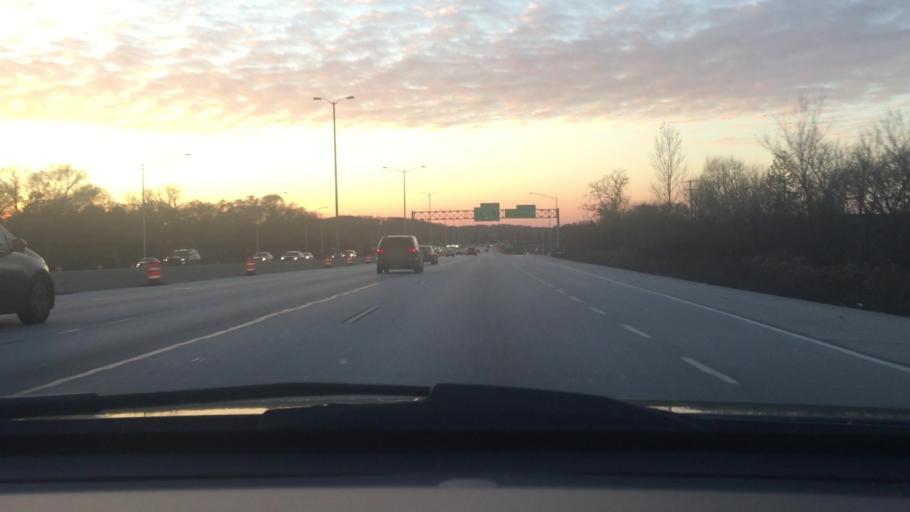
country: US
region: Wisconsin
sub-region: Waukesha County
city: Elm Grove
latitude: 43.0245
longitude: -88.0997
